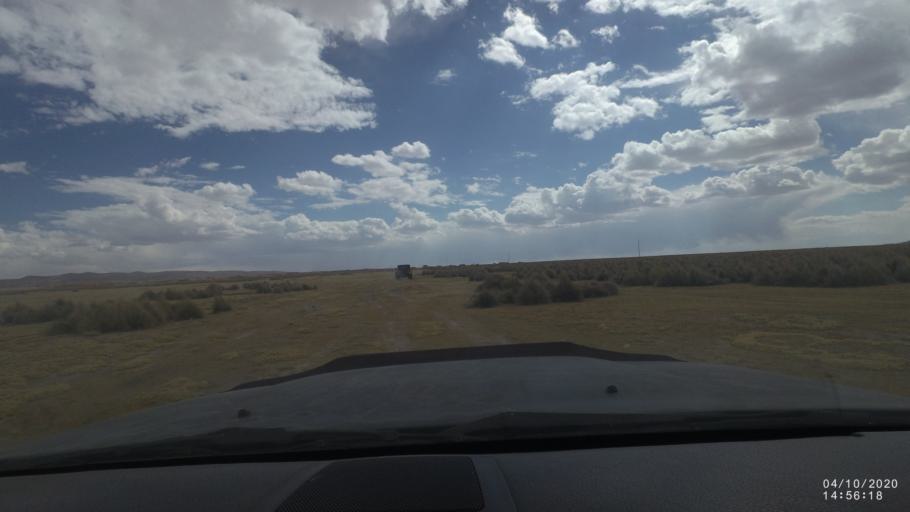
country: BO
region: Oruro
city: Poopo
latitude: -18.6843
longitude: -67.5156
